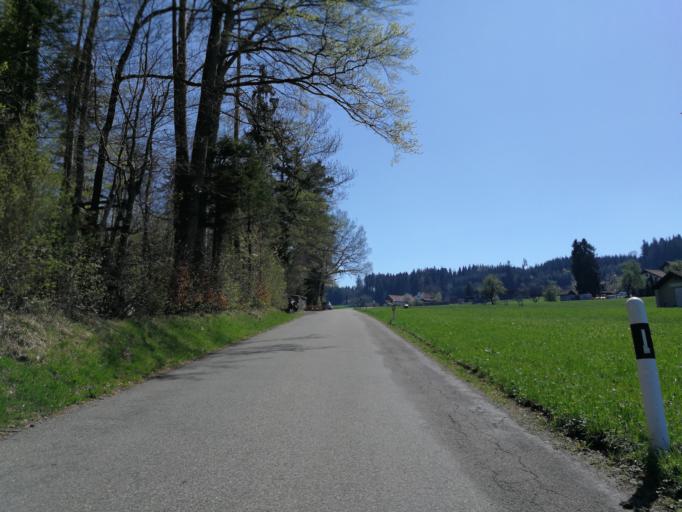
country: CH
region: Zurich
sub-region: Bezirk Uster
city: Hinteregg
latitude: 47.3085
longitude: 8.6613
